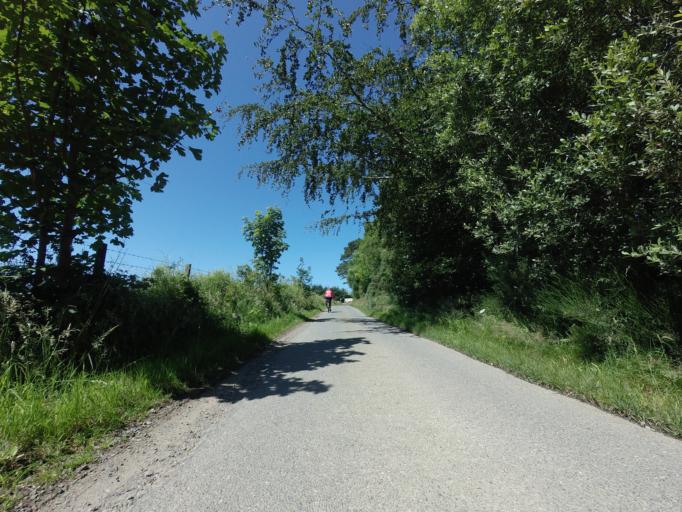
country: GB
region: Scotland
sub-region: Aberdeenshire
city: Macduff
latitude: 57.6433
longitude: -2.5070
